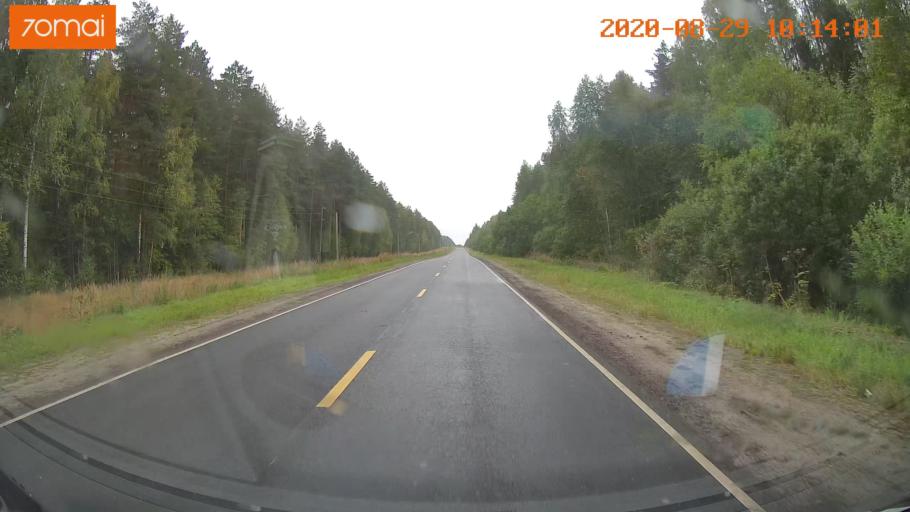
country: RU
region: Ivanovo
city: Yur'yevets
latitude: 57.3572
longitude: 42.7450
